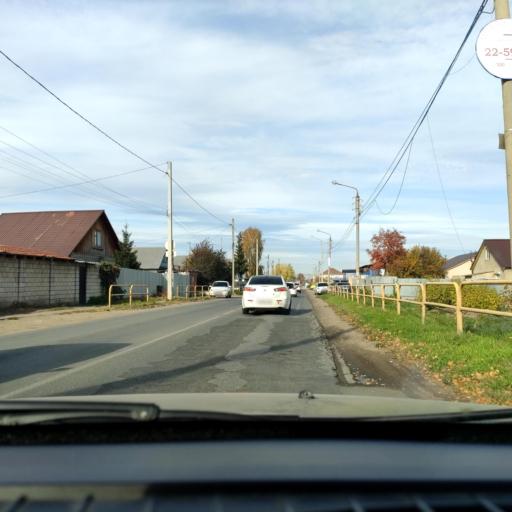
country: RU
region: Samara
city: Tol'yatti
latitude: 53.5351
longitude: 49.4287
